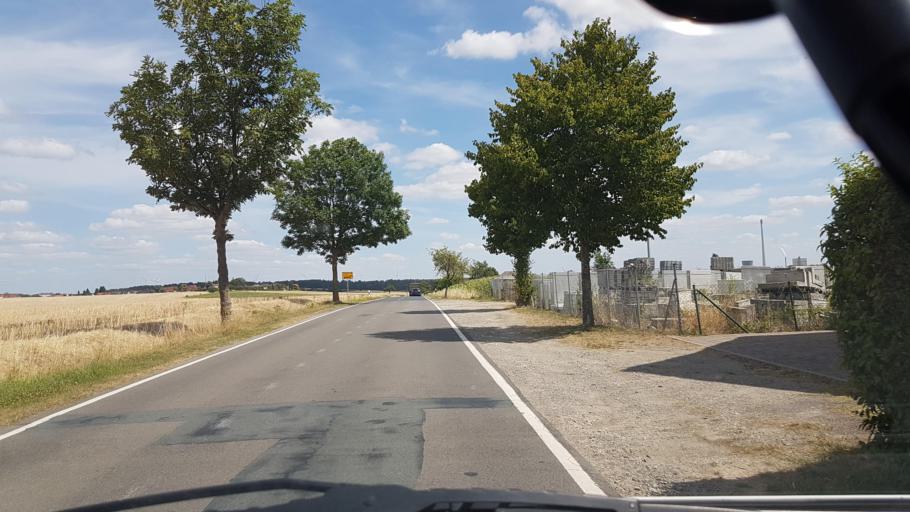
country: DE
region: Lower Saxony
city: Warberg
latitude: 52.1826
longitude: 10.9262
